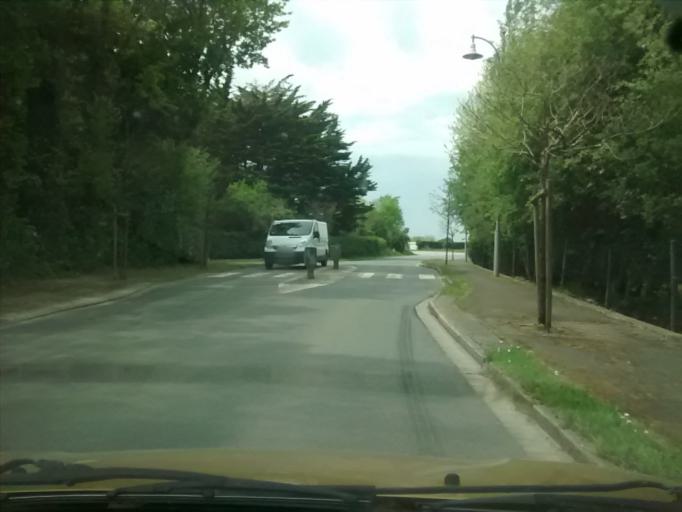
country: FR
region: Brittany
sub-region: Departement du Morbihan
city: Berric
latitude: 47.6302
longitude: -2.5284
